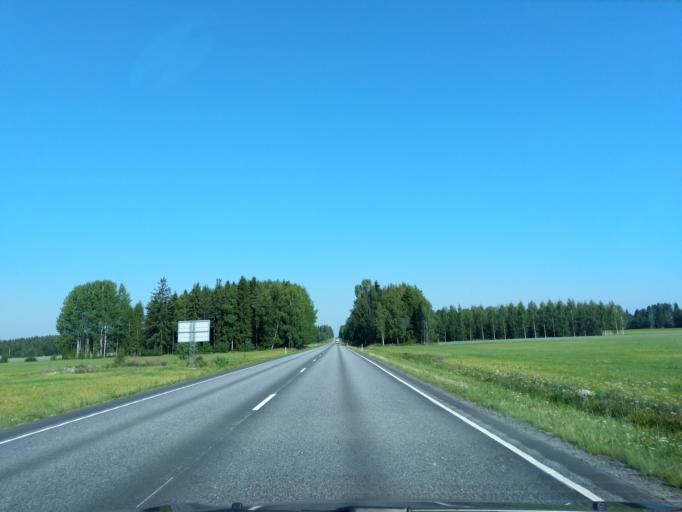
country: FI
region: Varsinais-Suomi
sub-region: Loimaa
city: Alastaro
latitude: 61.0662
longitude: 22.9297
